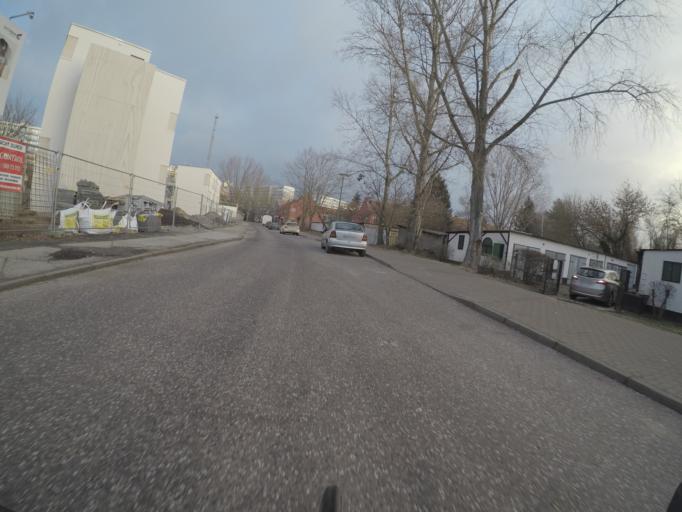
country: DE
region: Berlin
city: Karlshorst
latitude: 52.4932
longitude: 13.5192
